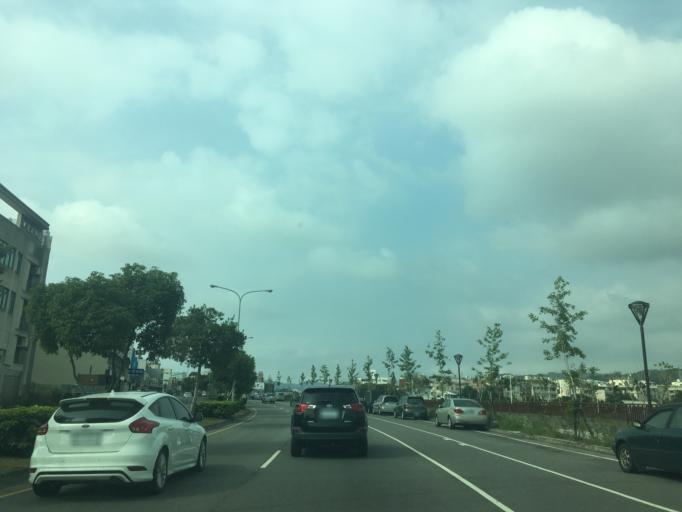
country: TW
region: Taiwan
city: Fengyuan
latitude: 24.2394
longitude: 120.7278
